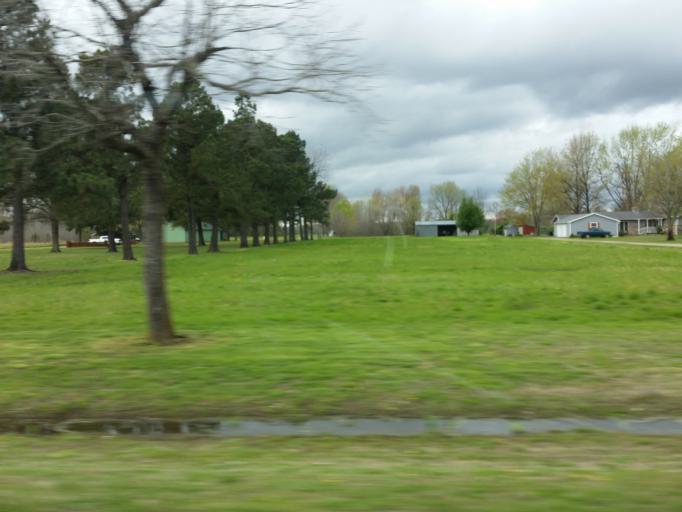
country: US
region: Missouri
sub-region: Butler County
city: Poplar Bluff
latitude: 36.6445
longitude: -90.5202
